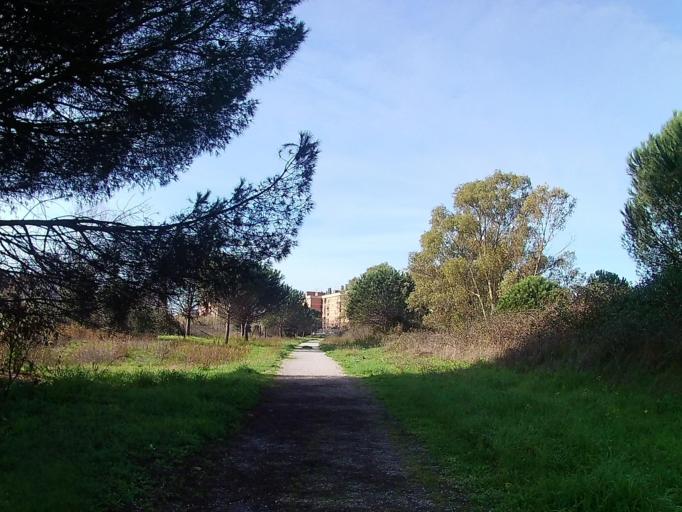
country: IT
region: Latium
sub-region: Citta metropolitana di Roma Capitale
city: Lido di Ostia
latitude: 41.7420
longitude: 12.2671
